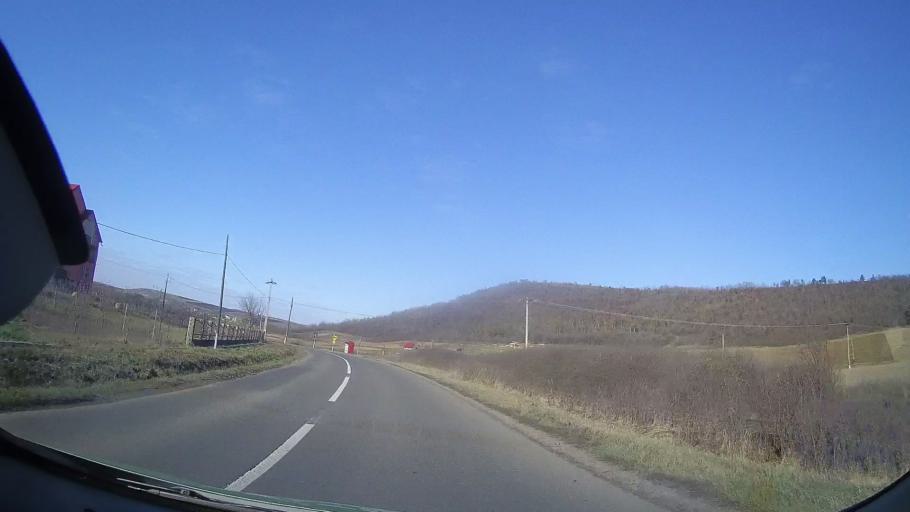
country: RO
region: Mures
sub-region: Comuna Mihesu de Campie
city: Mihesu de Campie
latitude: 46.6697
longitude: 24.1728
